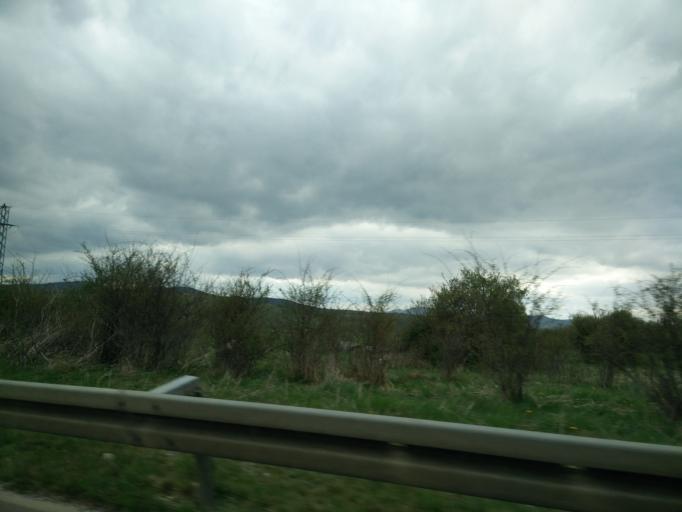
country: HR
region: Zadarska
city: Gracac
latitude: 44.5406
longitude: 15.7537
